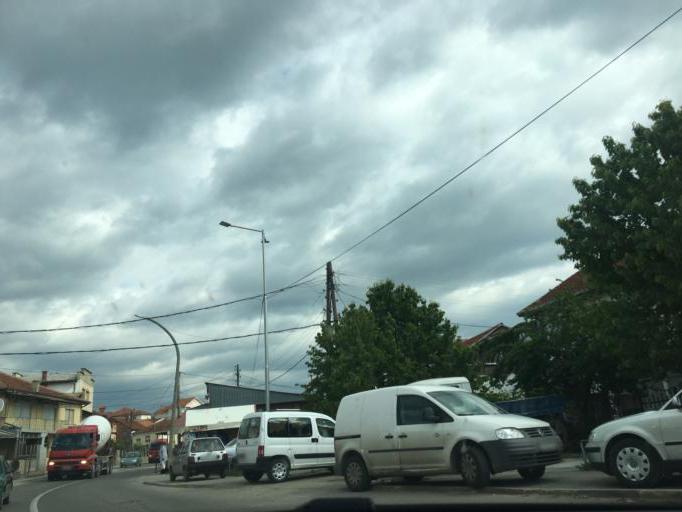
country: MK
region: Resen
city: Resen
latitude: 41.0927
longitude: 21.0115
